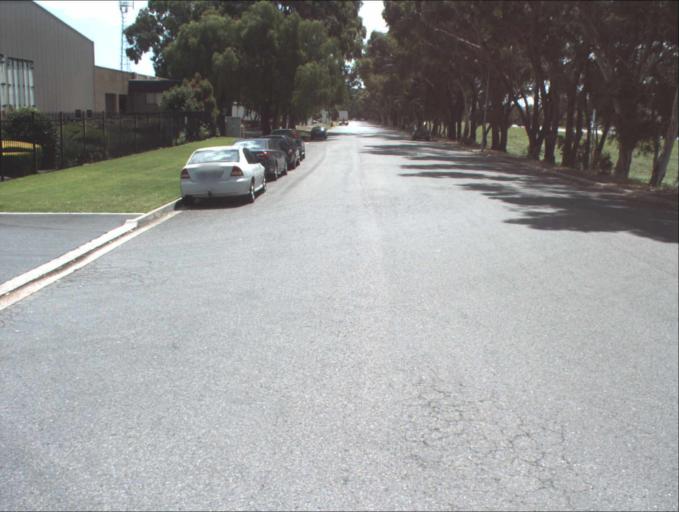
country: AU
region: South Australia
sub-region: Port Adelaide Enfield
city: Blair Athol
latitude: -34.8556
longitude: 138.5737
